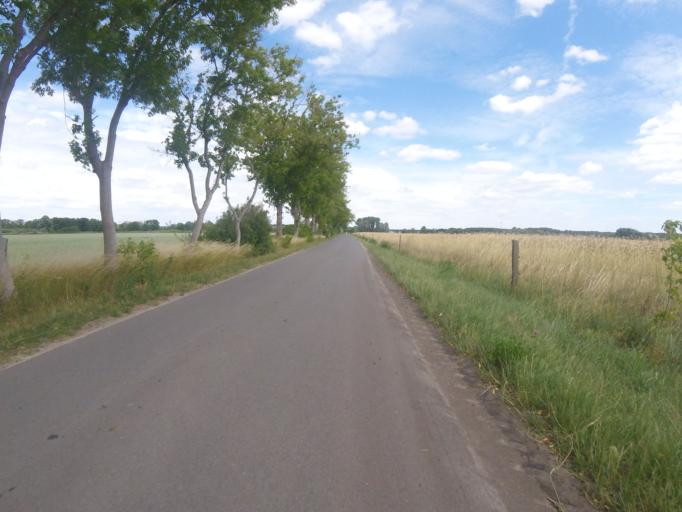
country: DE
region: Brandenburg
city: Bestensee
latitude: 52.2323
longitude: 13.7052
